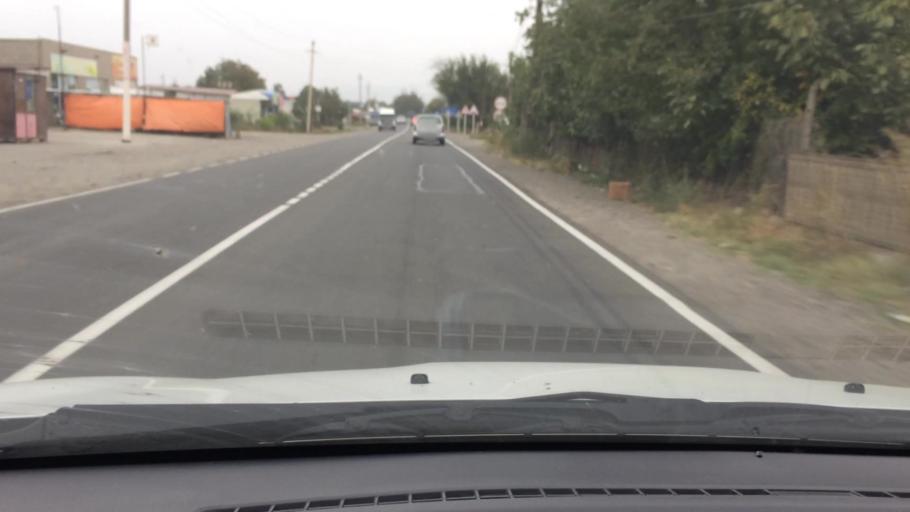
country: GE
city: Naghvarevi
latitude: 41.3747
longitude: 44.8346
